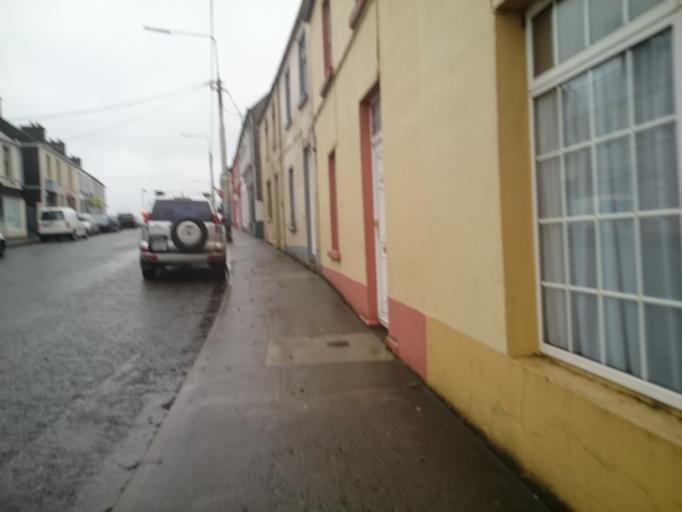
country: IE
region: Connaught
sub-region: Maigh Eo
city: Ballyhaunis
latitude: 53.7619
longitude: -8.7636
